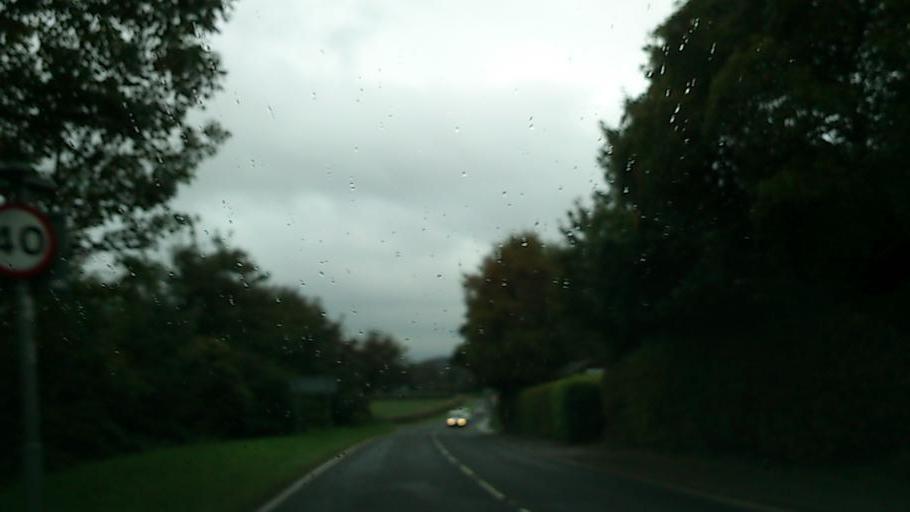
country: GB
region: Wales
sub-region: County of Ceredigion
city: Bow Street
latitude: 52.5067
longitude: -3.9784
